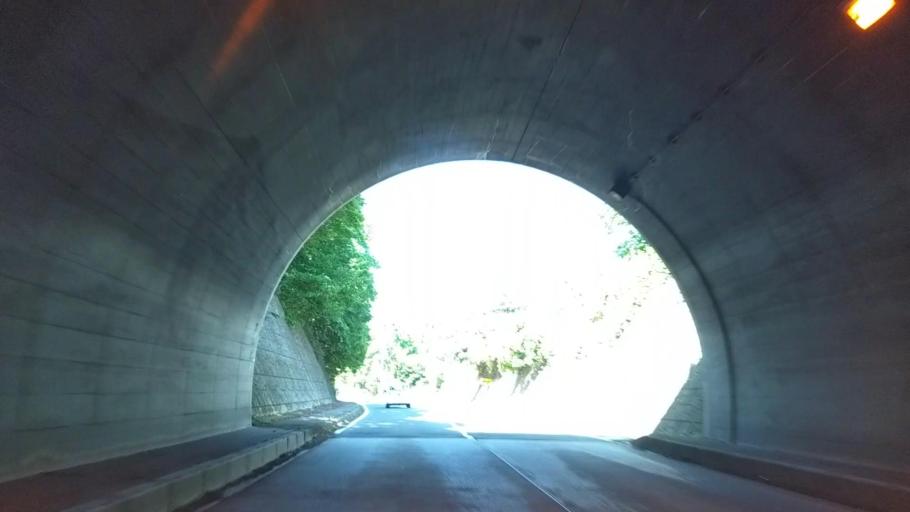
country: JP
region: Nagano
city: Komoro
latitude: 36.3442
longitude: 138.4398
